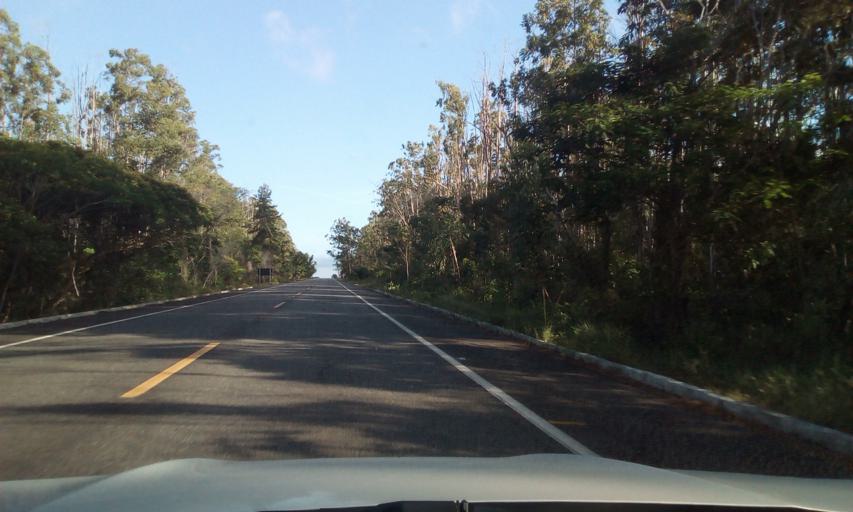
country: BR
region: Bahia
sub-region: Entre Rios
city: Entre Rios
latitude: -12.3230
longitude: -37.9043
